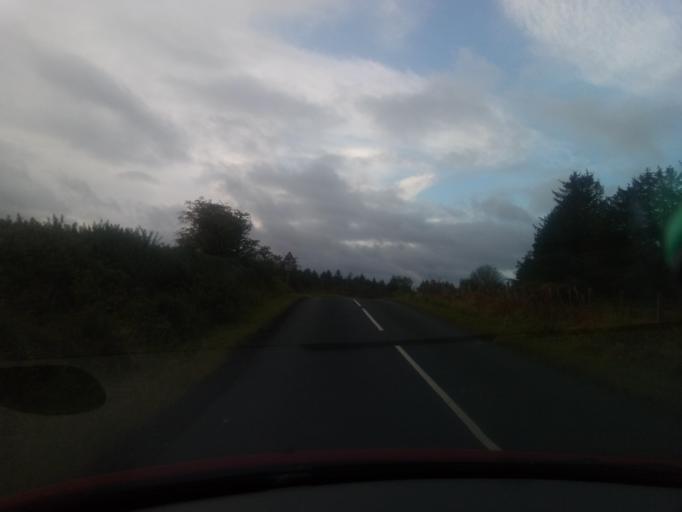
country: GB
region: Scotland
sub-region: The Scottish Borders
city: Jedburgh
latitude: 55.4391
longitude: -2.5959
